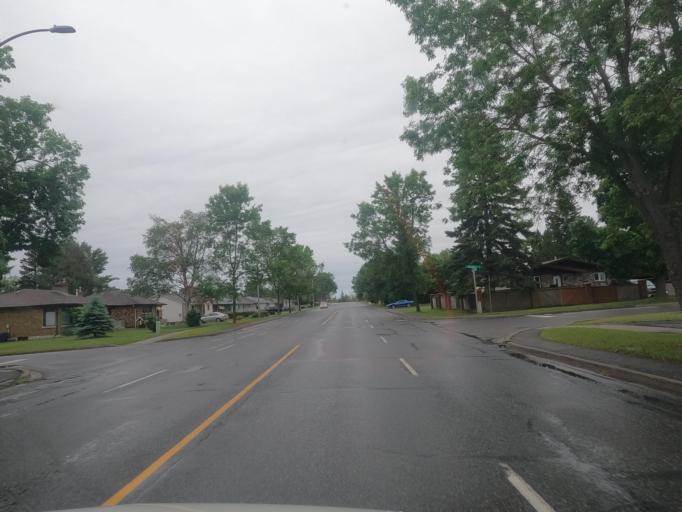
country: CA
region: Ontario
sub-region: Thunder Bay District
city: Thunder Bay
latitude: 48.4609
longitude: -89.1823
